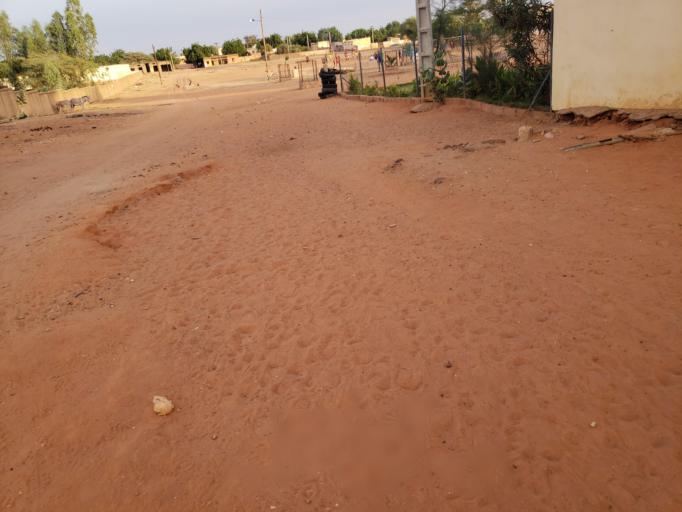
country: SN
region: Louga
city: Ndibene Dahra
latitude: 15.4000
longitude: -15.1111
